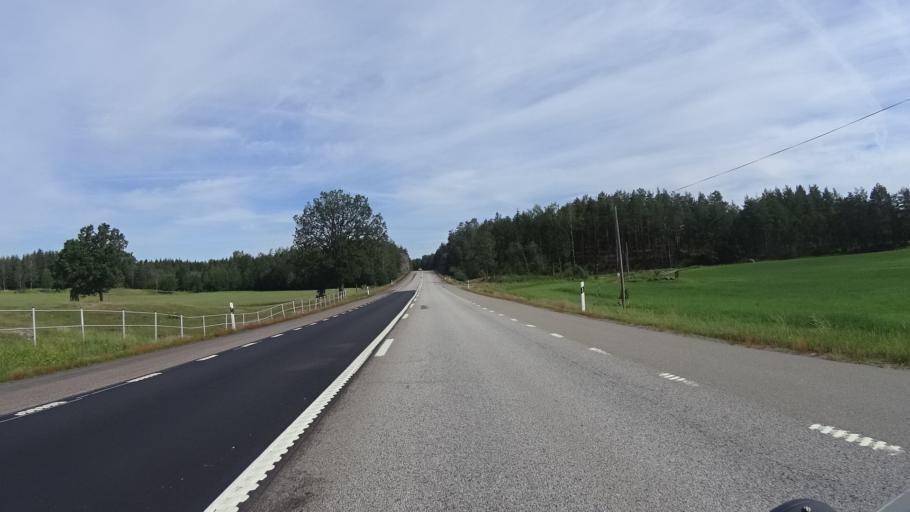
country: SE
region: Kalmar
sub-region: Vasterviks Kommun
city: Ankarsrum
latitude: 57.6113
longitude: 16.4727
